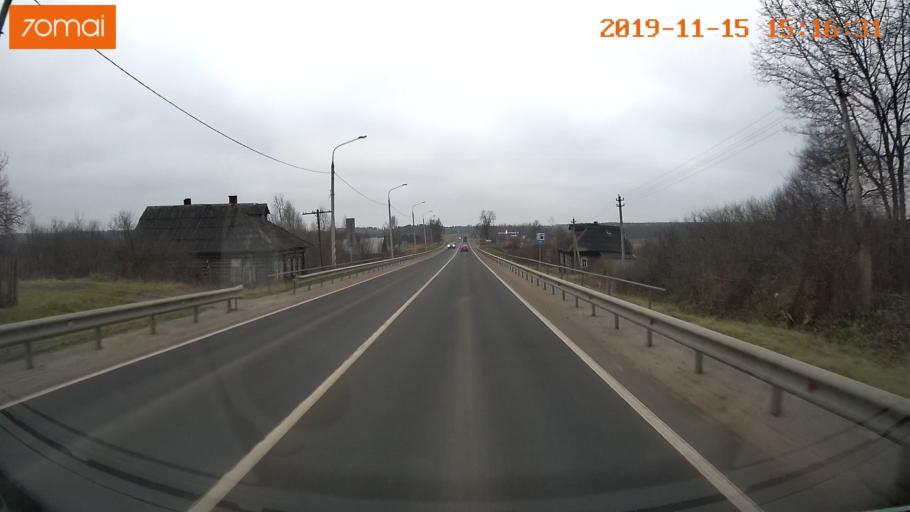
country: RU
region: Jaroslavl
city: Danilov
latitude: 58.2723
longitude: 40.1904
